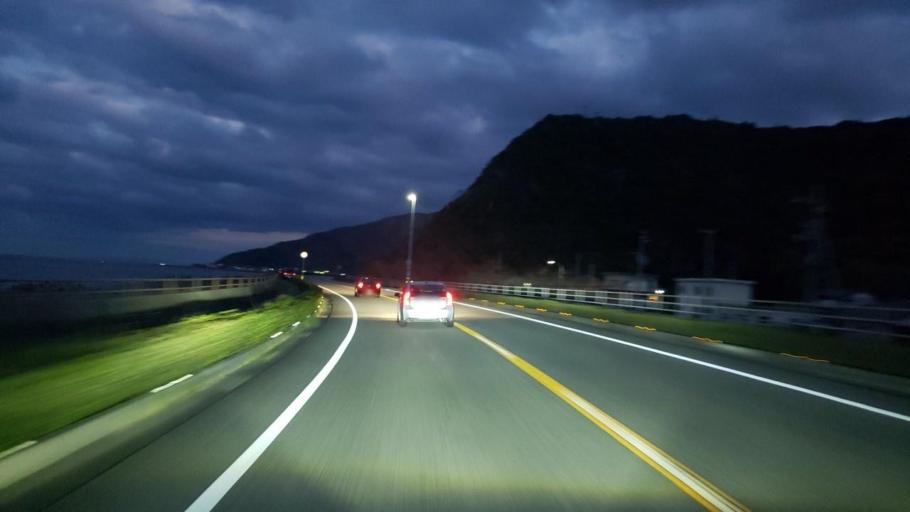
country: JP
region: Tokushima
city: Ishii
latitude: 34.2074
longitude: 134.4647
